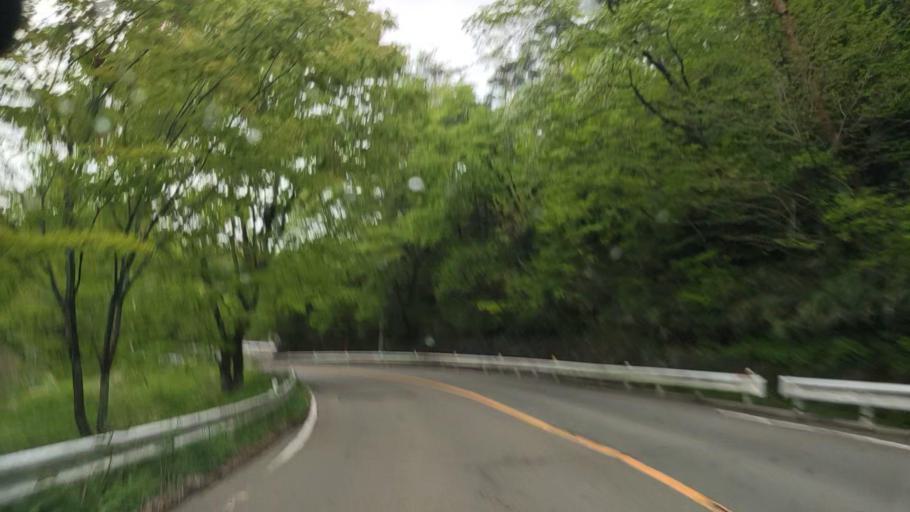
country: JP
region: Miyagi
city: Sendai
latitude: 38.2563
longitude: 140.8439
